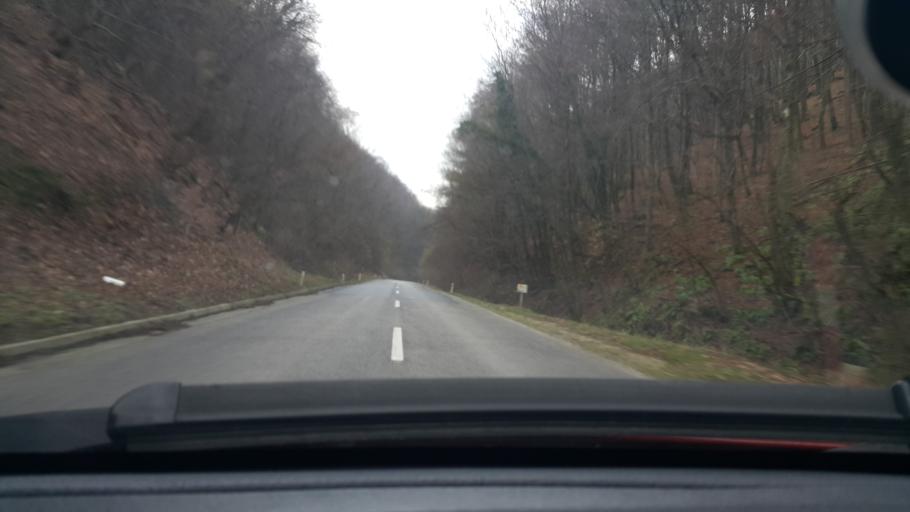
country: SI
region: Bistrica ob Sotli
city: Bistrica ob Sotli
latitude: 46.0323
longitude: 15.6872
